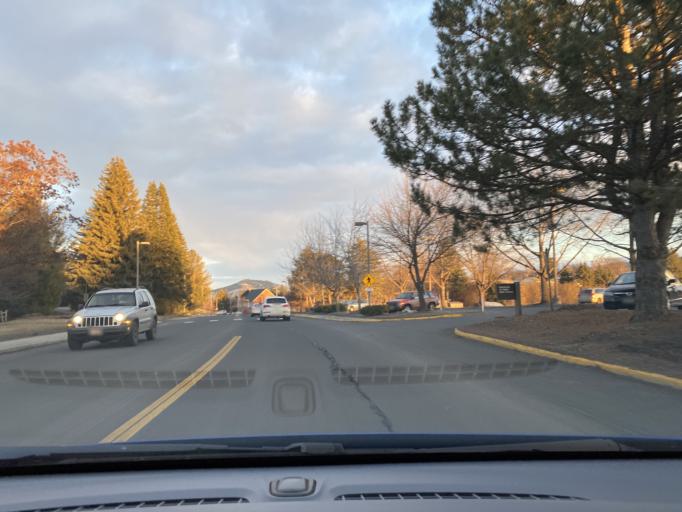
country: US
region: Idaho
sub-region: Latah County
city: Moscow
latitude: 46.7237
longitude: -117.0163
